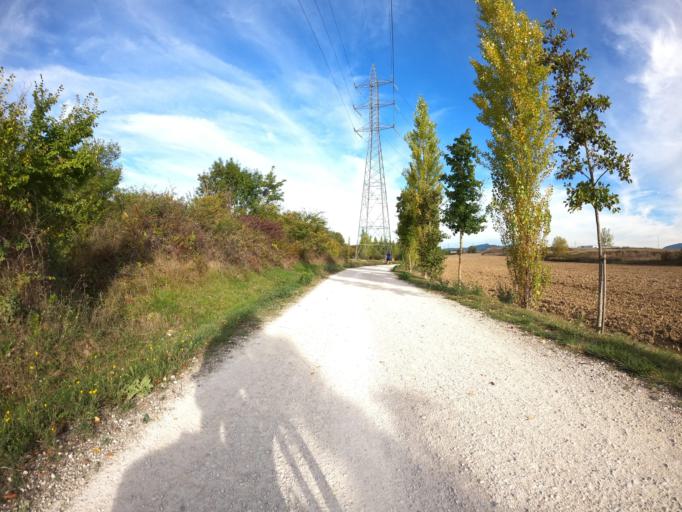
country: ES
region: Navarre
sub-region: Provincia de Navarra
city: Orkoien
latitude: 42.8033
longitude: -1.7109
